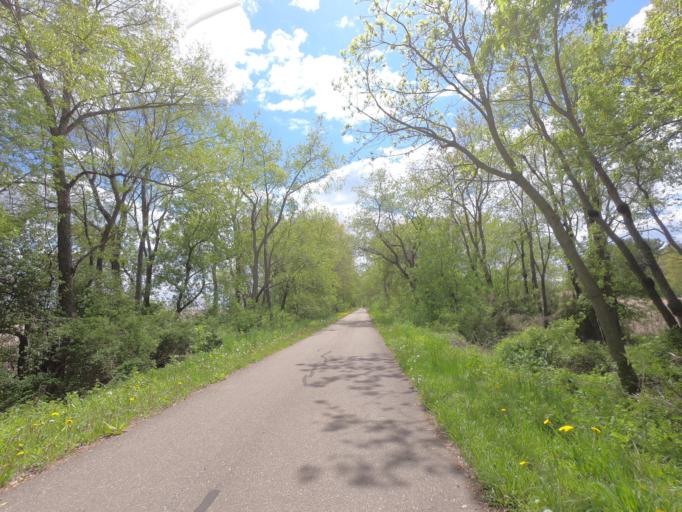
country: US
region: Wisconsin
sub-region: Dane County
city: Fitchburg
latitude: 42.9541
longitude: -89.4738
